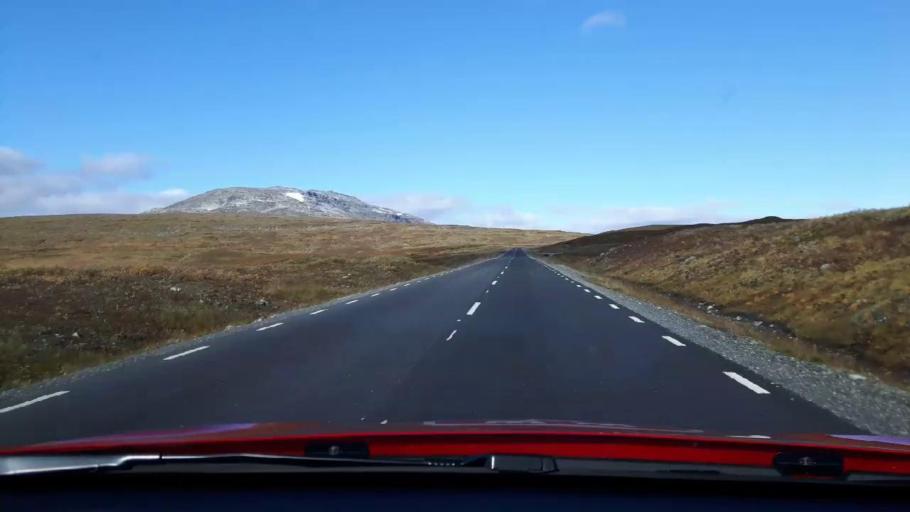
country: NO
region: Nordland
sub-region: Hattfjelldal
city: Hattfjelldal
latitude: 65.0333
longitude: 14.3338
